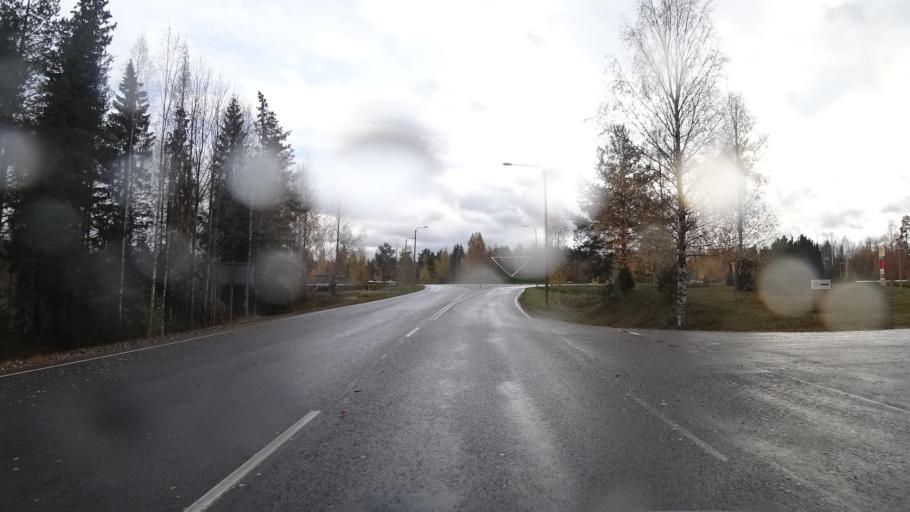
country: FI
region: Southern Savonia
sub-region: Mikkeli
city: Kangasniemi
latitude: 62.0044
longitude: 26.6574
